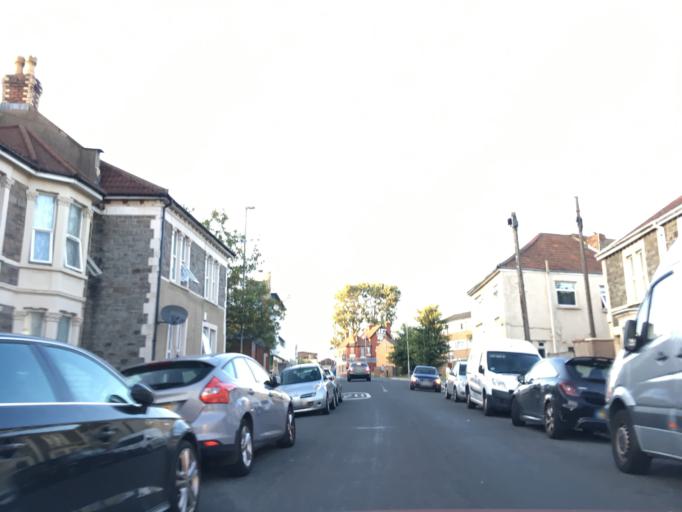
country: GB
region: England
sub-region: Bristol
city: Bristol
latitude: 51.4571
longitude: -2.5549
